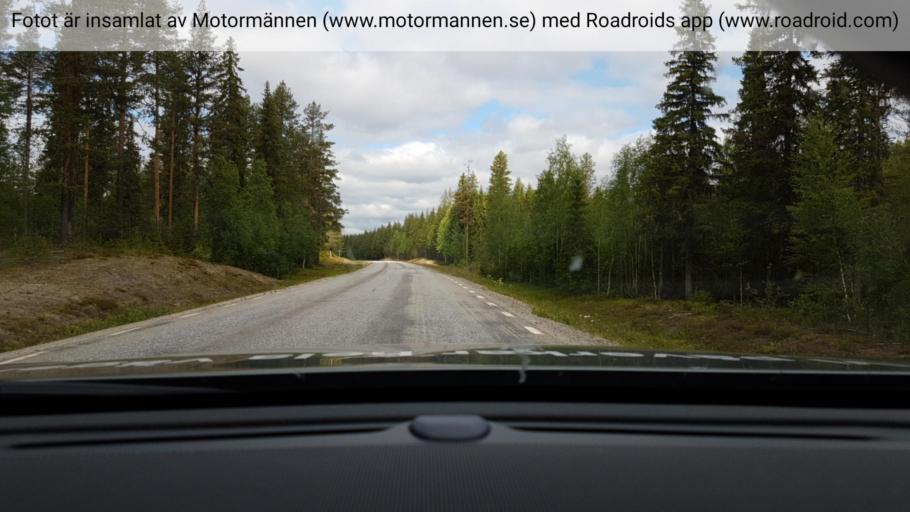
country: SE
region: Vaesterbotten
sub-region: Mala Kommun
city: Mala
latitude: 64.9456
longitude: 18.6190
